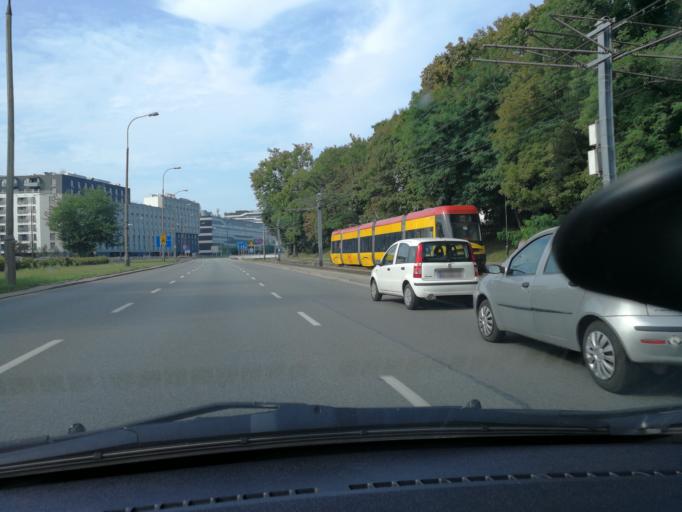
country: PL
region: Masovian Voivodeship
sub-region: Warszawa
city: Ochota
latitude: 52.2275
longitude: 20.9462
